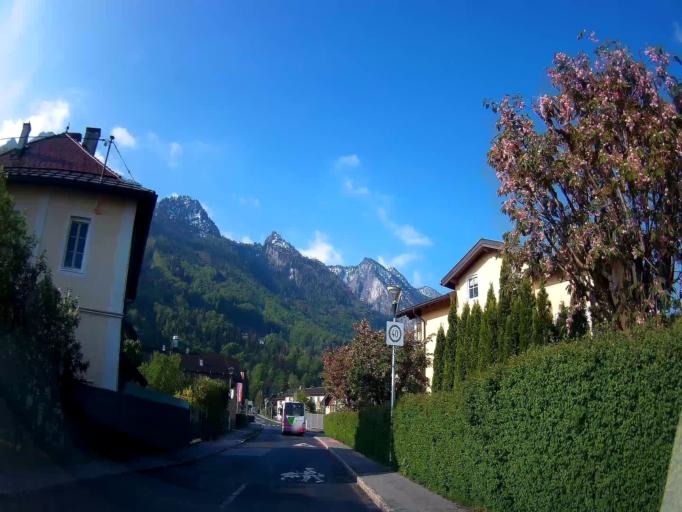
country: AT
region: Salzburg
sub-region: Politischer Bezirk Salzburg-Umgebung
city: Grodig
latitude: 47.7459
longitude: 12.9926
